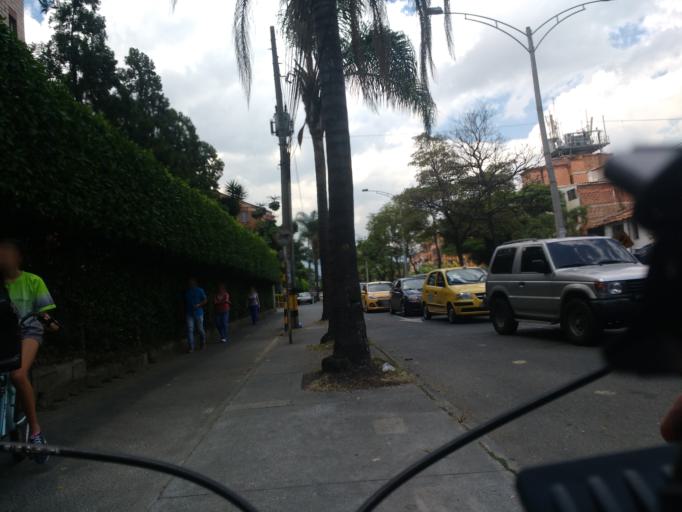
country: CO
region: Antioquia
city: Medellin
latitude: 6.2285
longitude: -75.5911
